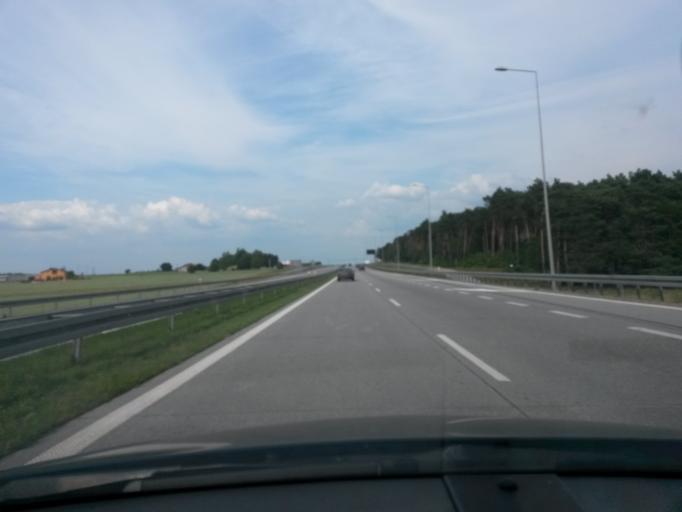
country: PL
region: Lodz Voivodeship
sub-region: Powiat tomaszowski
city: Czerniewice
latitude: 51.6825
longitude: 20.1955
